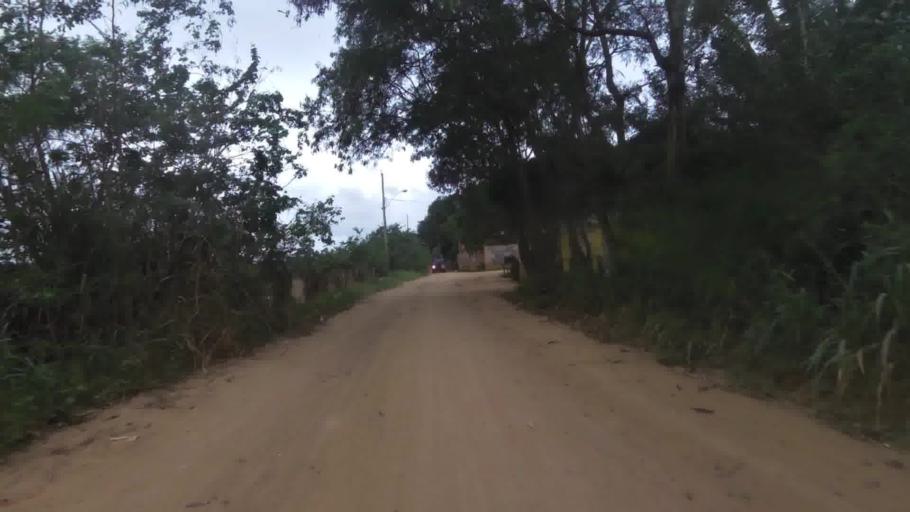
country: BR
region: Espirito Santo
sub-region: Guarapari
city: Guarapari
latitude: -20.5232
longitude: -40.4708
